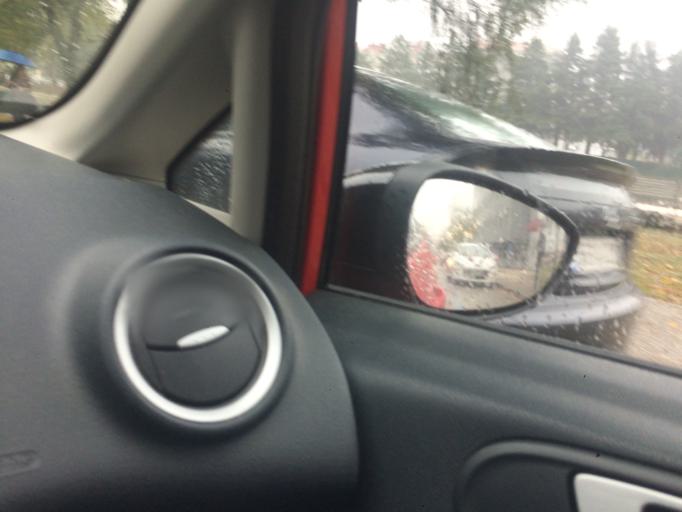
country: ES
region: Galicia
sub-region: Provincia da Coruna
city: Santiago de Compostela
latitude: 42.8739
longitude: -8.5569
